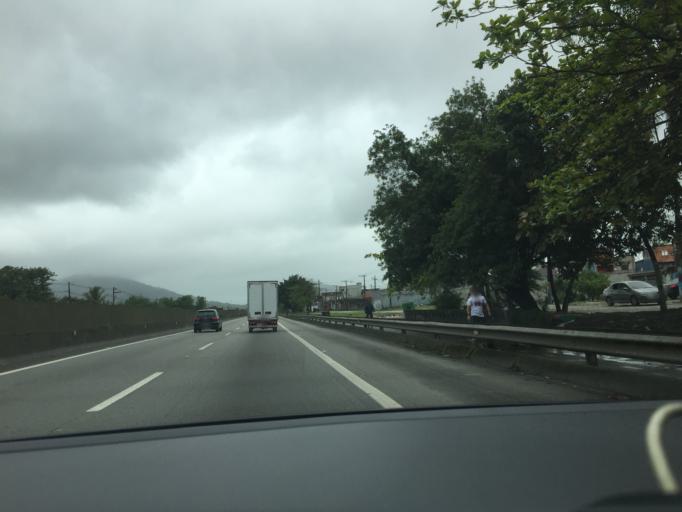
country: BR
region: Sao Paulo
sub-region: Guaruja
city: Guaruja
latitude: -23.9542
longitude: -46.2759
